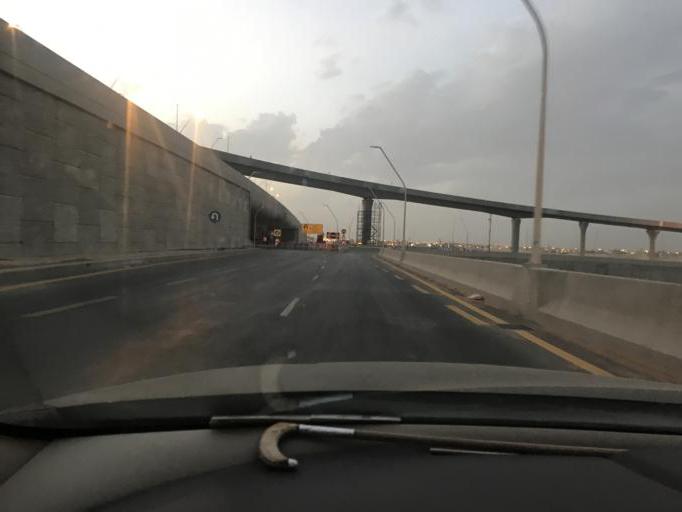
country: SA
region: Ar Riyad
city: Riyadh
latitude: 24.8418
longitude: 46.6542
